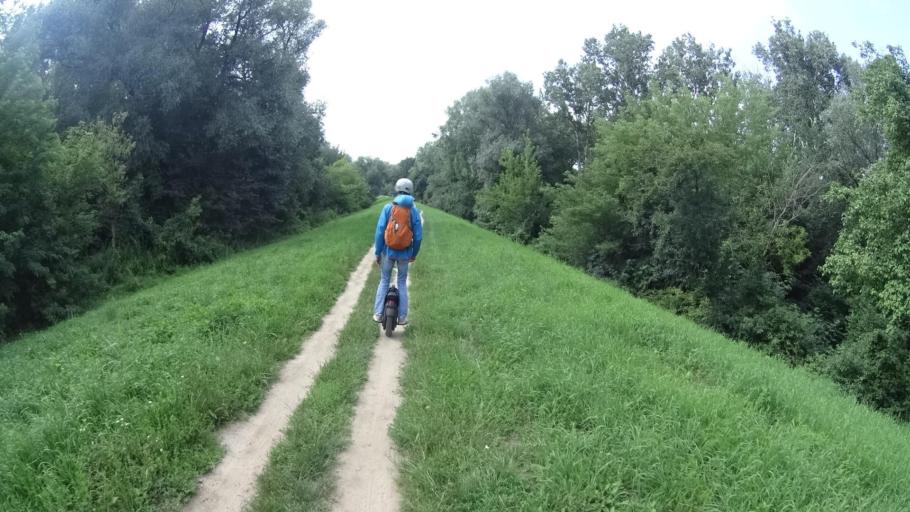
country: PL
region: Masovian Voivodeship
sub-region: Powiat legionowski
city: Jablonna
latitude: 52.3704
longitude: 20.9145
